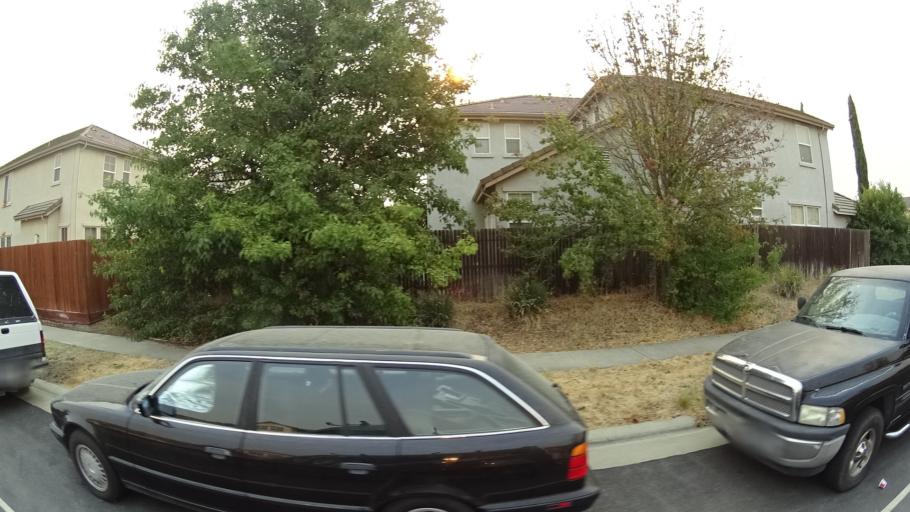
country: US
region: California
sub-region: Sacramento County
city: Laguna
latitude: 38.3831
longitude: -121.4437
